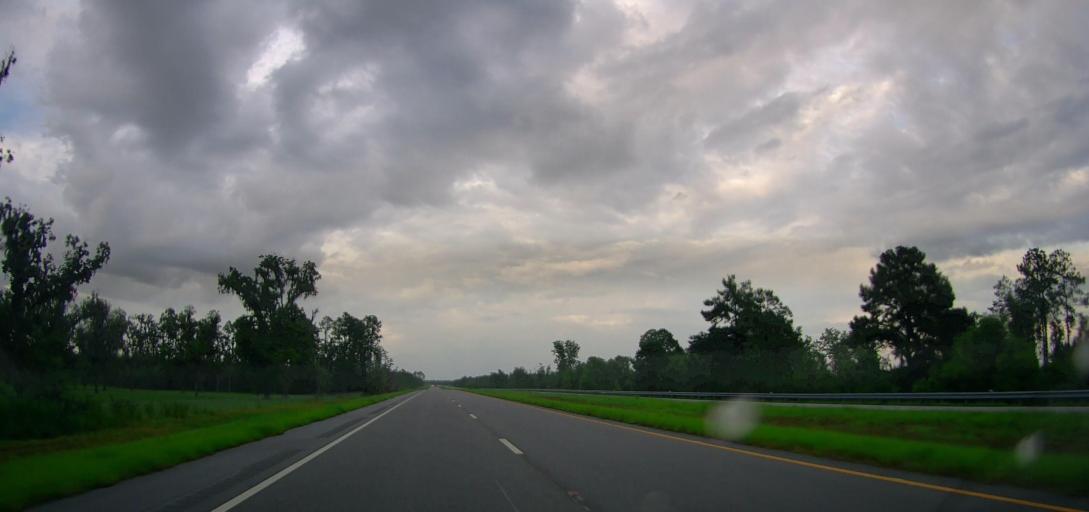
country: US
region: Georgia
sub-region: Ware County
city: Deenwood
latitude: 31.1516
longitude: -82.4441
